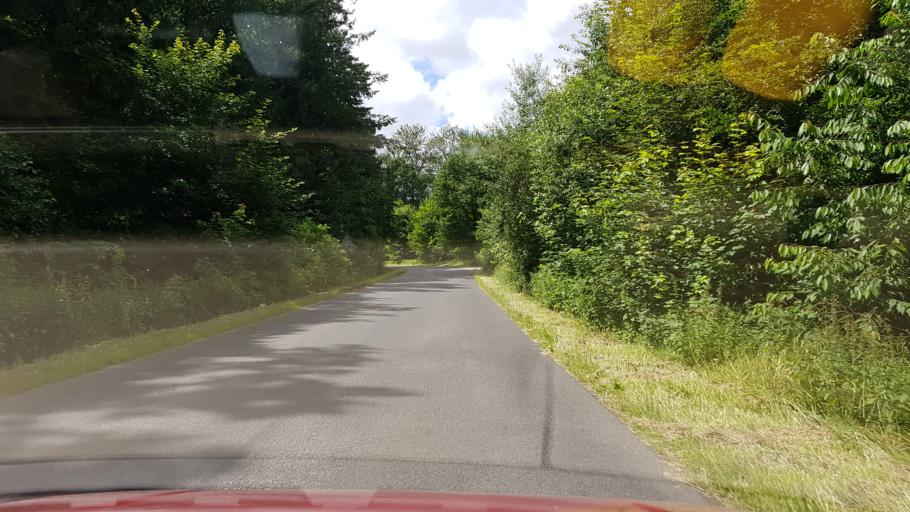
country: PL
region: West Pomeranian Voivodeship
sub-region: Powiat koszalinski
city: Mielno
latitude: 54.1693
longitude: 15.9869
